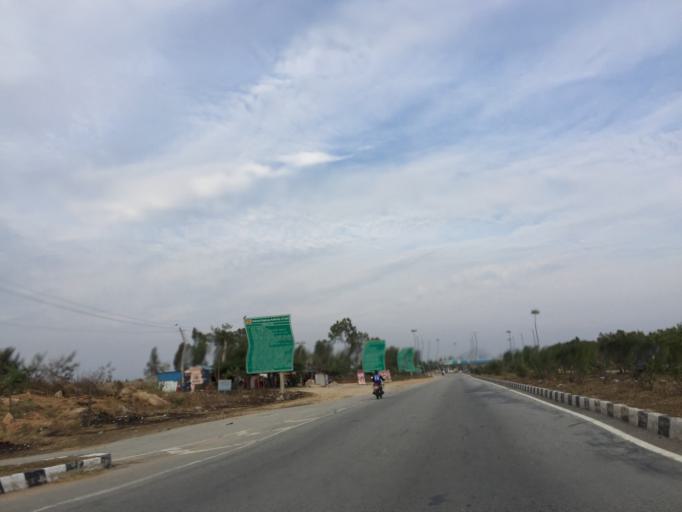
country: IN
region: Karnataka
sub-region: Kolar
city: Mulbagal
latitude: 13.1475
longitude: 78.2865
